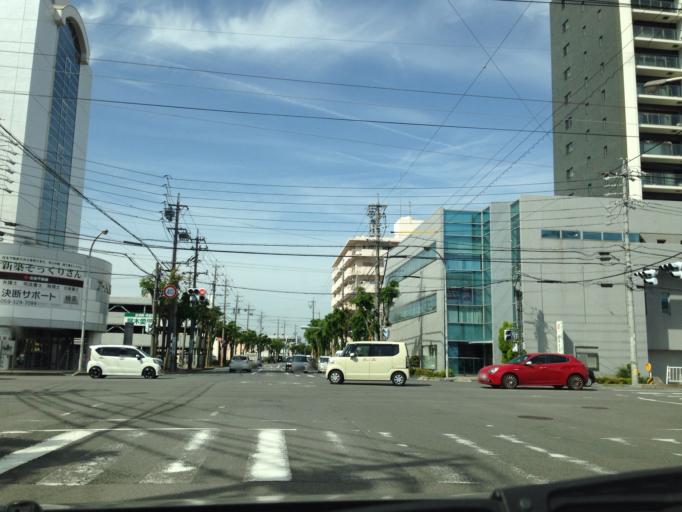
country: JP
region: Mie
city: Yokkaichi
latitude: 34.9716
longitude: 136.6160
